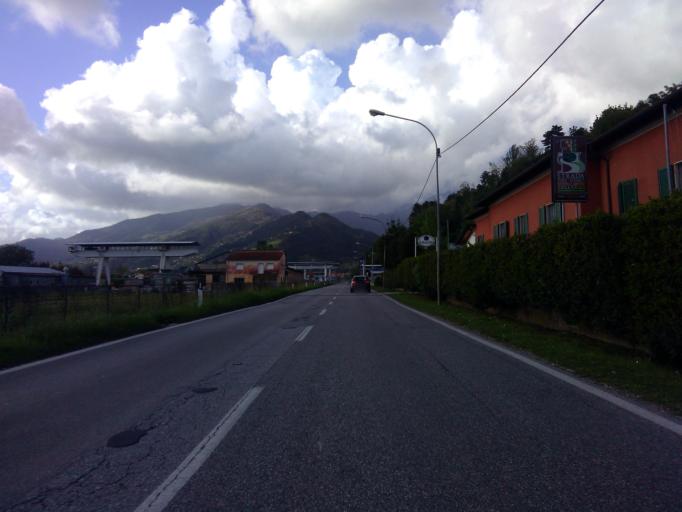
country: IT
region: Tuscany
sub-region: Provincia di Lucca
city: Ripa-Pozzi-Querceta-Ponterosso
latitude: 43.9708
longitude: 10.2205
